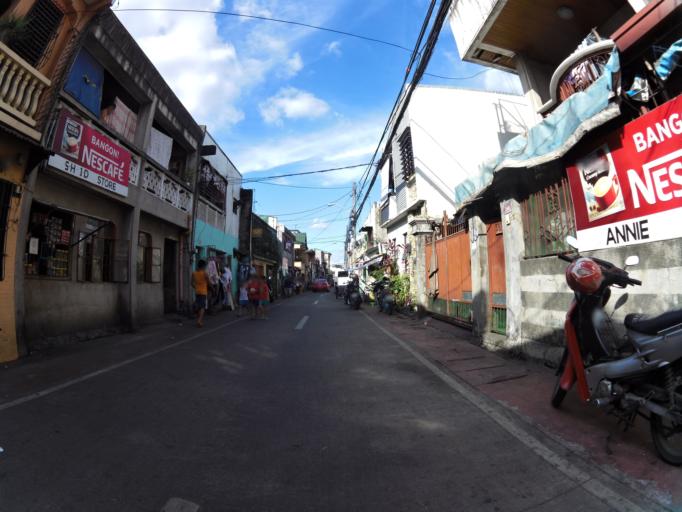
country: PH
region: Metro Manila
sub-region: Marikina
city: Calumpang
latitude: 14.6393
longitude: 121.0978
